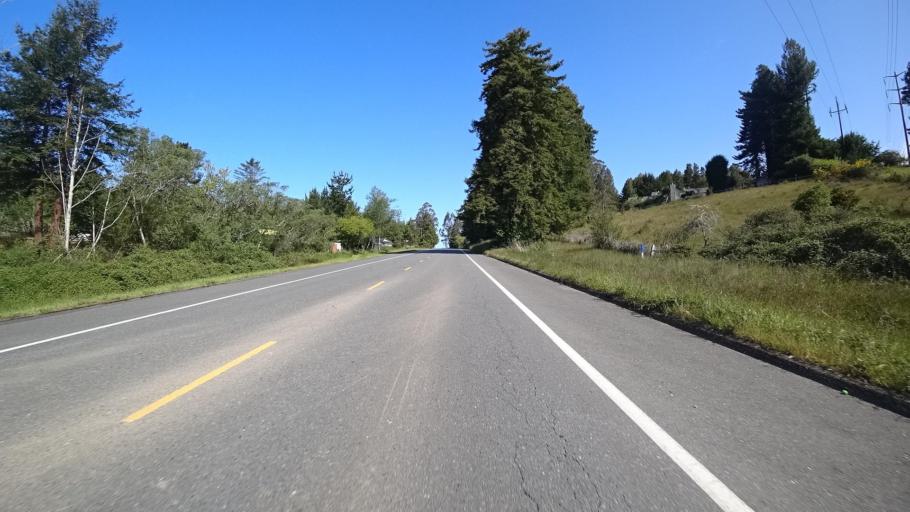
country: US
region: California
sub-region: Humboldt County
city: Bayside
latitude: 40.8129
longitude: -124.0875
